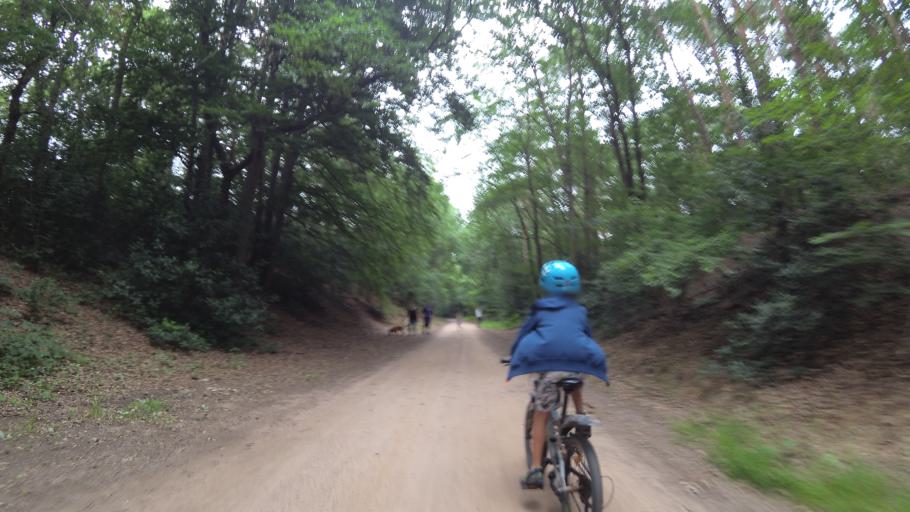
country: DE
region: Lower Saxony
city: Fresenburg
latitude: 52.8802
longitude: 7.3007
